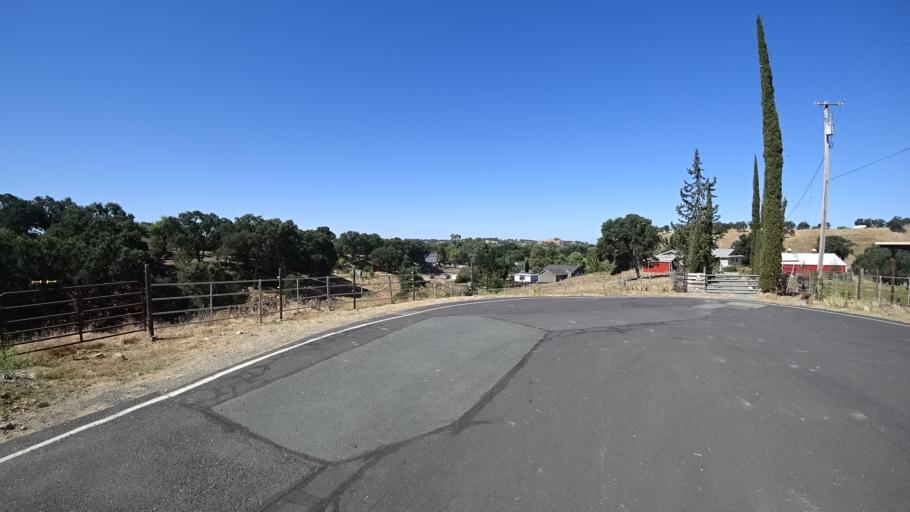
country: US
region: California
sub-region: Calaveras County
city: Rancho Calaveras
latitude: 38.1013
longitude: -120.8763
